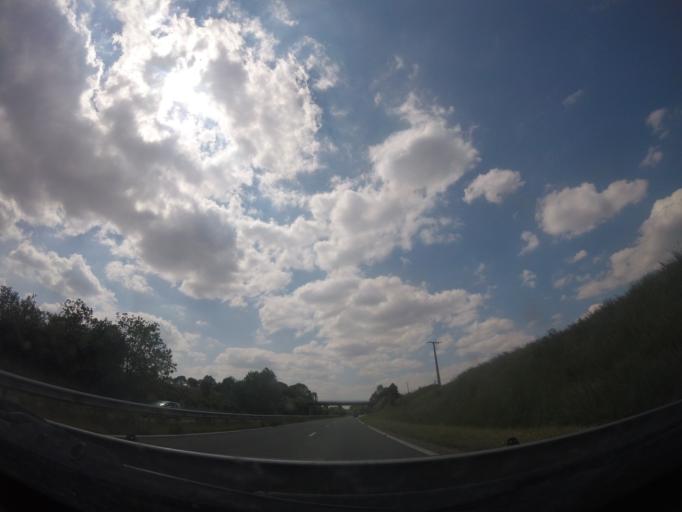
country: FR
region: Poitou-Charentes
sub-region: Departement de la Charente-Maritime
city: Saint-Porchaire
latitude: 45.8132
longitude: -0.7791
